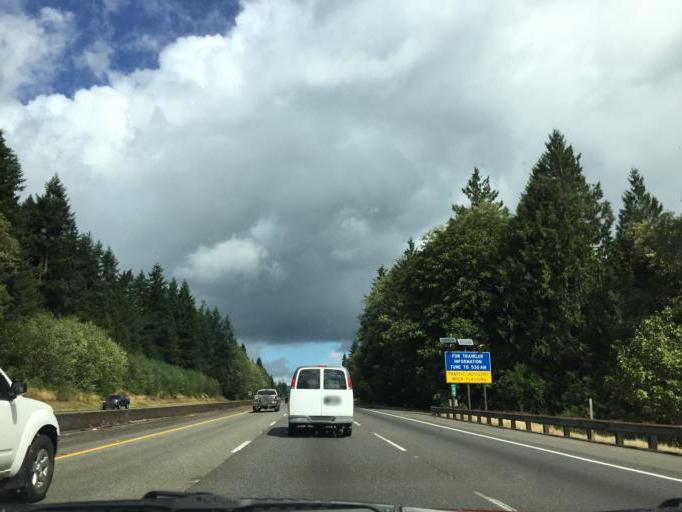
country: US
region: Washington
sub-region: Lewis County
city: Winlock
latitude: 46.4832
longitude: -122.8803
